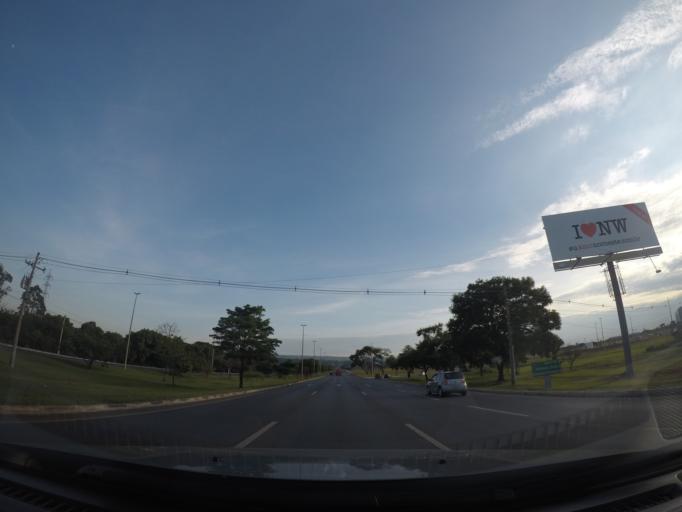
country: BR
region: Federal District
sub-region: Brasilia
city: Brasilia
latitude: -15.7402
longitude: -47.9168
